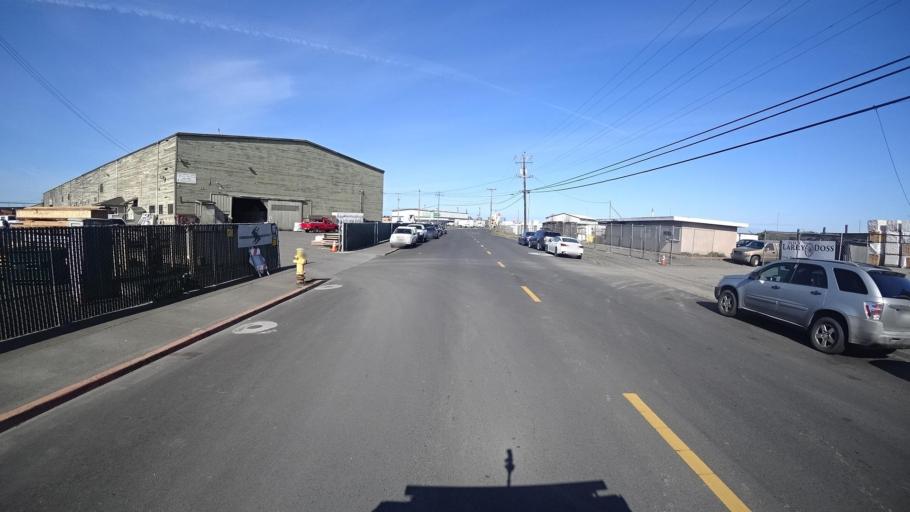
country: US
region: California
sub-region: Humboldt County
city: Eureka
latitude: 40.7983
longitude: -124.1800
